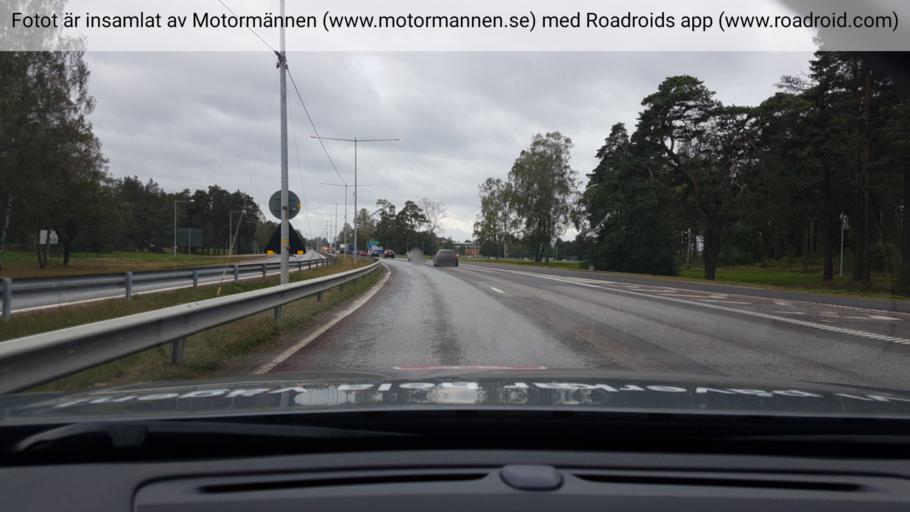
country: SE
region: Vaermland
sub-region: Karlstads Kommun
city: Karlstad
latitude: 59.3957
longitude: 13.4984
